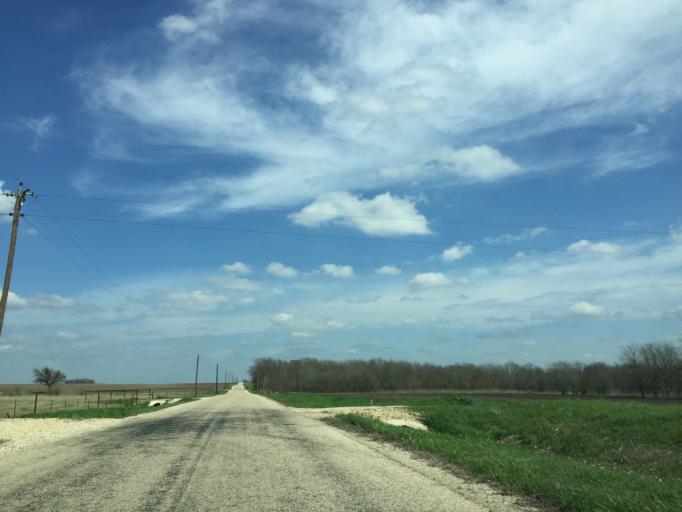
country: US
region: Texas
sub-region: Milam County
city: Thorndale
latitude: 30.5517
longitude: -97.2632
